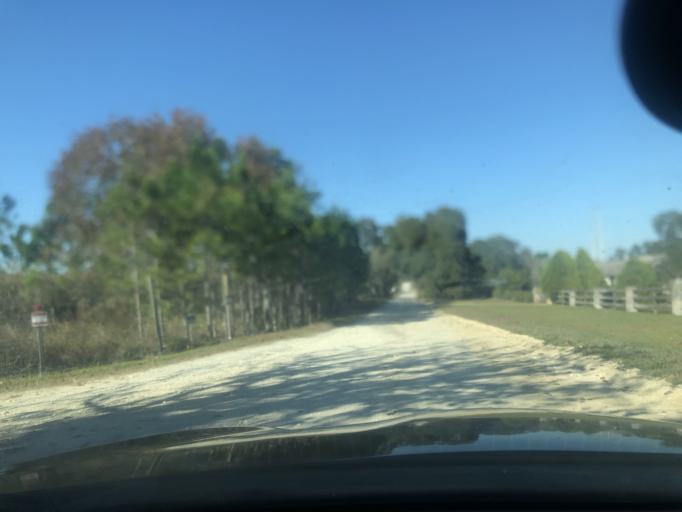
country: US
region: Florida
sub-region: Citrus County
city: Lecanto
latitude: 28.8186
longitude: -82.5180
